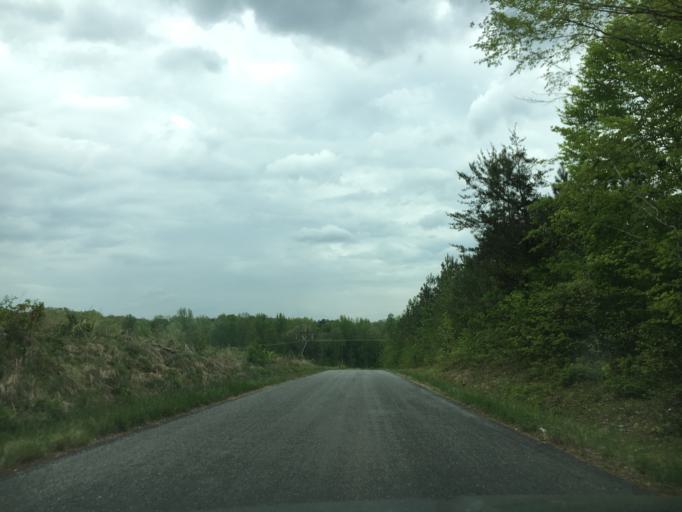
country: US
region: Virginia
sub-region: Halifax County
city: Halifax
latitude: 36.8000
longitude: -78.9311
